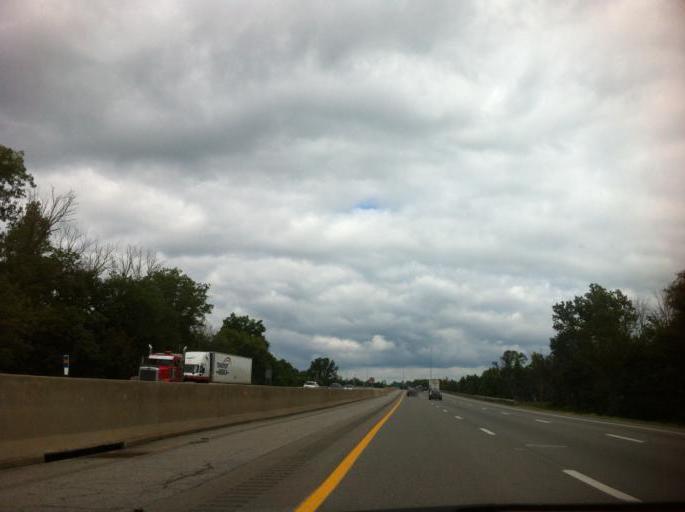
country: US
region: Ohio
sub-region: Trumbull County
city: Newton Falls
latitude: 41.2096
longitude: -80.9492
